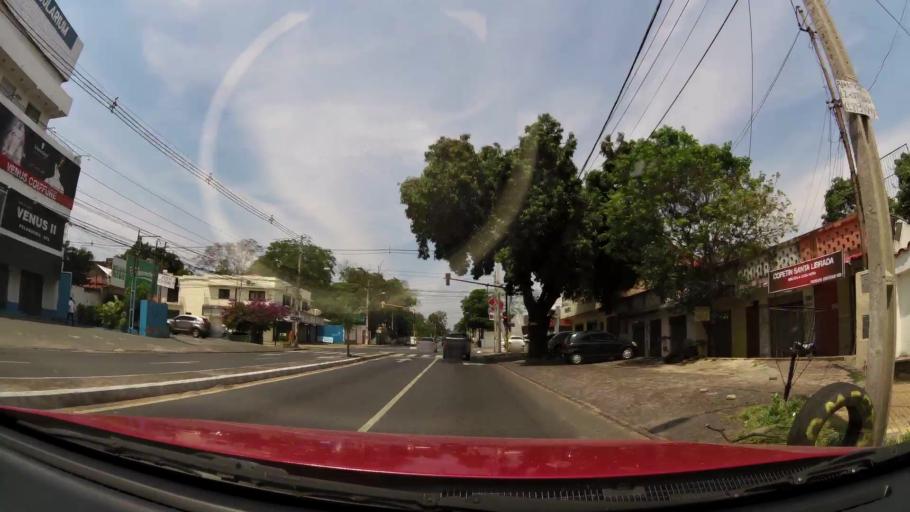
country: PY
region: Asuncion
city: Asuncion
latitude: -25.2988
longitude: -57.5936
